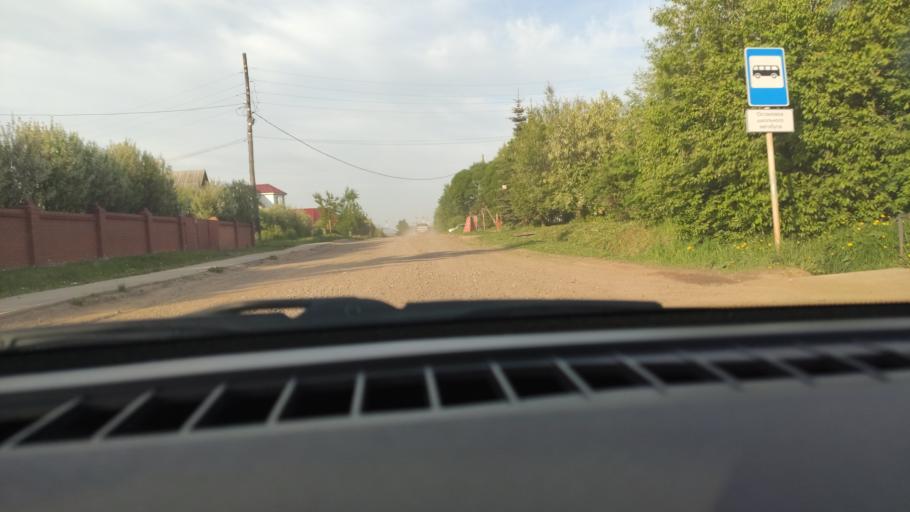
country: RU
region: Perm
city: Kultayevo
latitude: 57.9170
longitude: 55.9980
